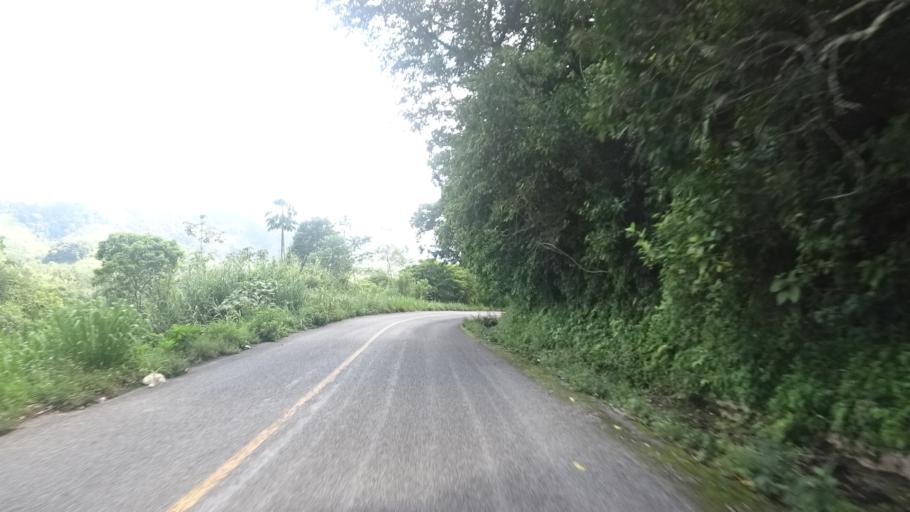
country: MX
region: Chiapas
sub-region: Palenque
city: Doctor Samuel Leon Brindis
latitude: 17.4445
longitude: -91.9670
